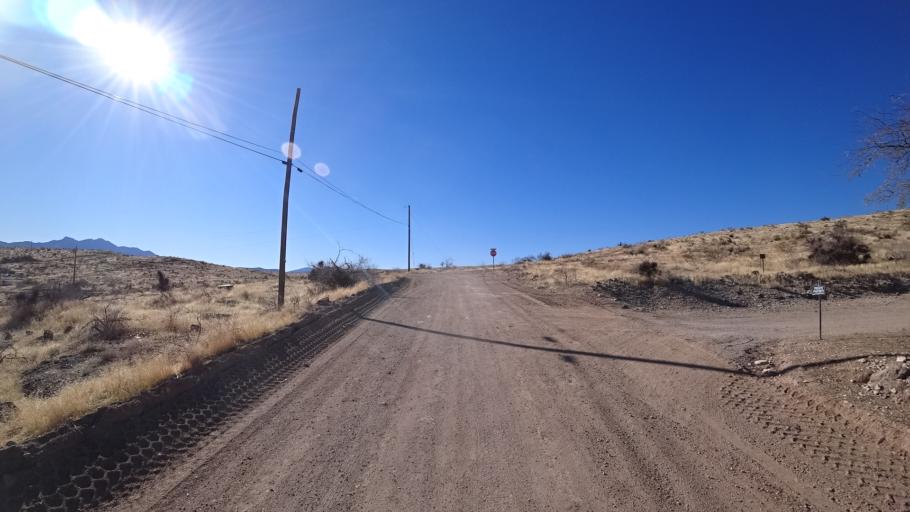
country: US
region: Arizona
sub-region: Mohave County
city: Kingman
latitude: 35.1848
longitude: -114.0579
